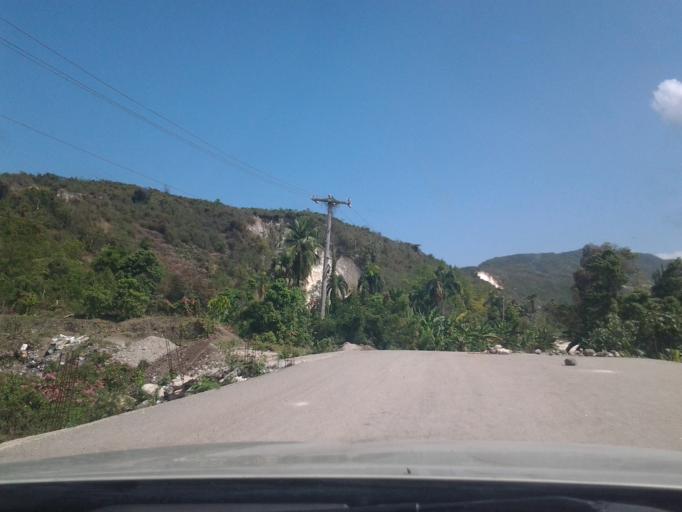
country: HT
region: Ouest
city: Tigwav
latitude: 18.4405
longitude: -72.8449
